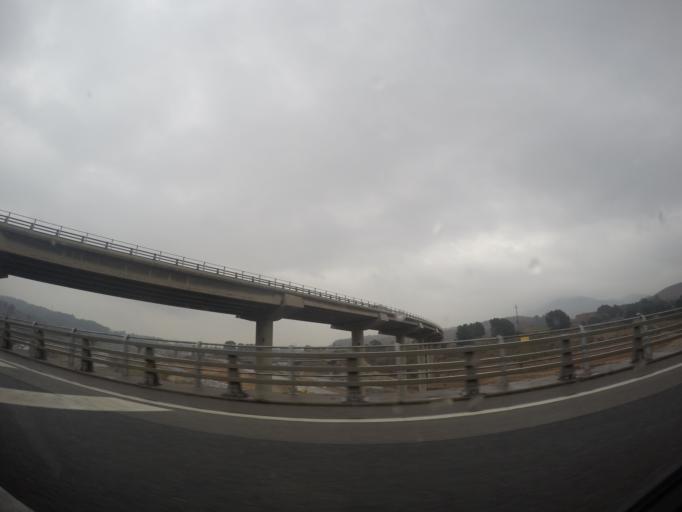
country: ES
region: Catalonia
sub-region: Provincia de Barcelona
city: Palleja
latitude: 41.4450
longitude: 1.9976
